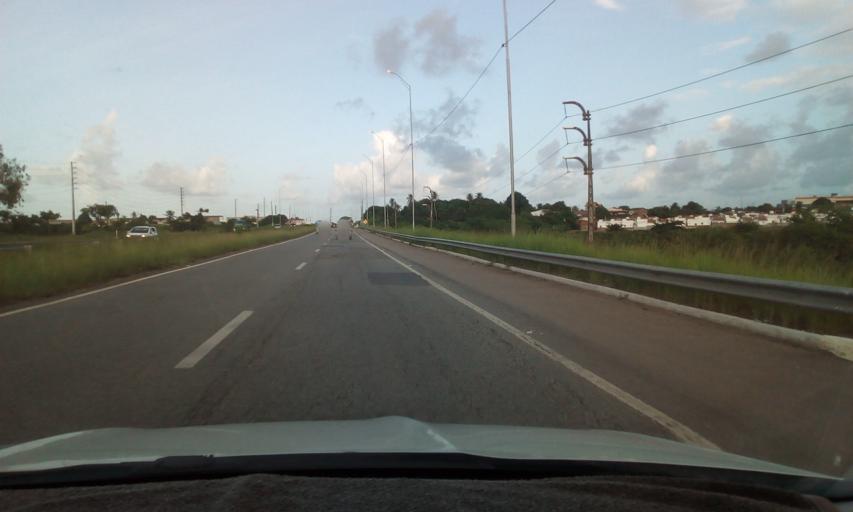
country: BR
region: Paraiba
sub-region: Santa Rita
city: Santa Rita
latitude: -7.1155
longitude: -34.9559
